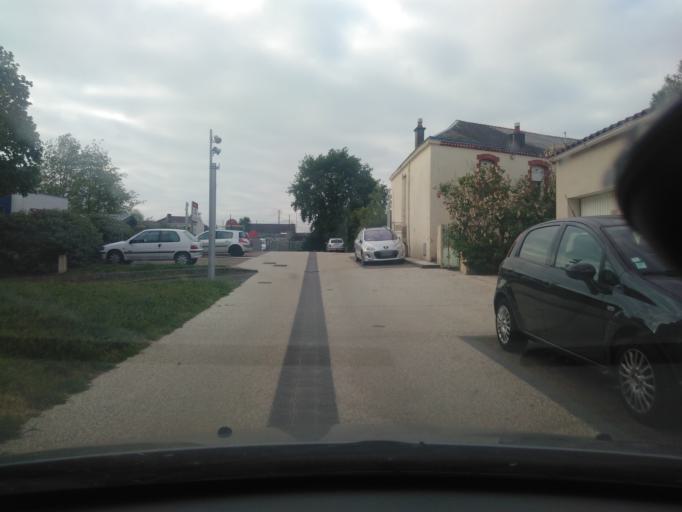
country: FR
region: Pays de la Loire
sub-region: Departement de la Vendee
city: La Roche-sur-Yon
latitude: 46.6799
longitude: -1.4336
